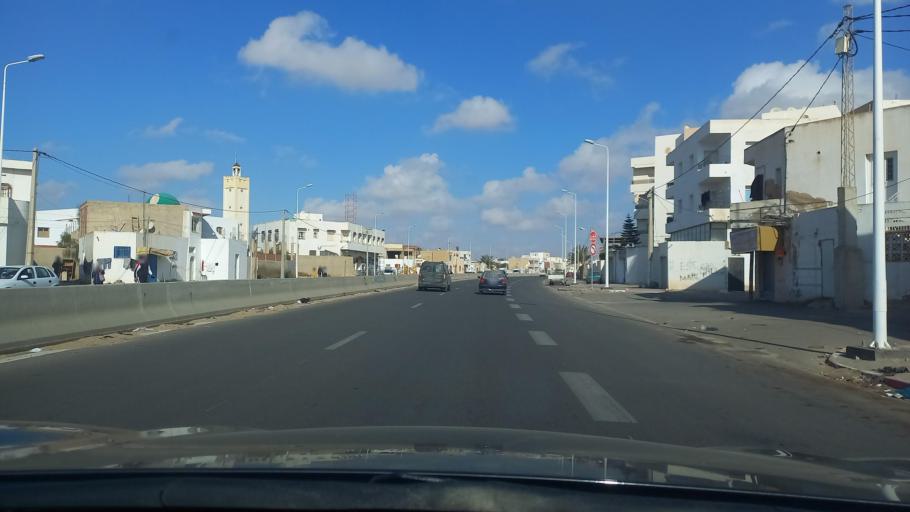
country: TN
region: Safaqis
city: Sfax
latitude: 34.7394
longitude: 10.7238
